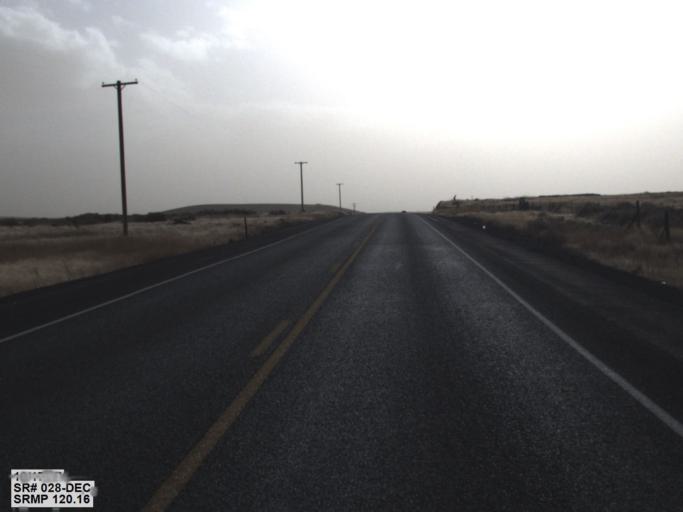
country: US
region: Washington
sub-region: Lincoln County
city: Davenport
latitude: 47.5076
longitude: -118.2255
